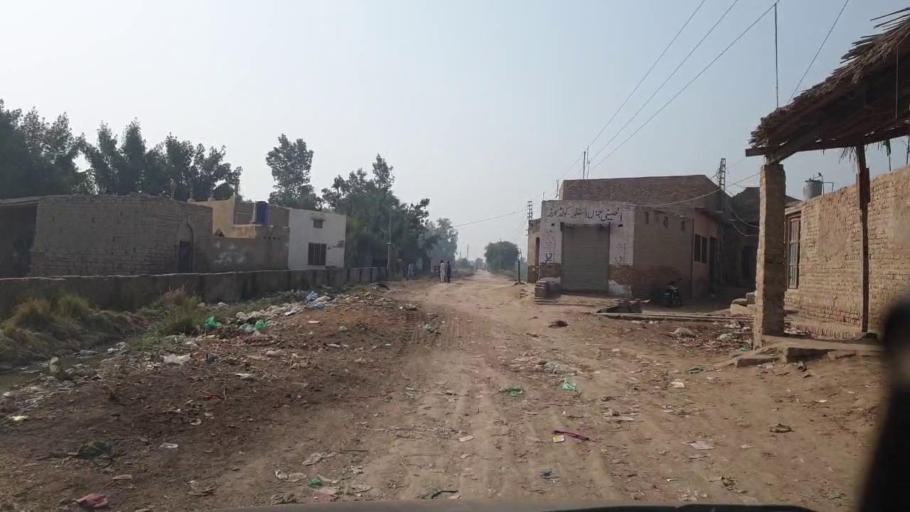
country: PK
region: Sindh
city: Shahdadpur
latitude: 26.0260
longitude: 68.5441
